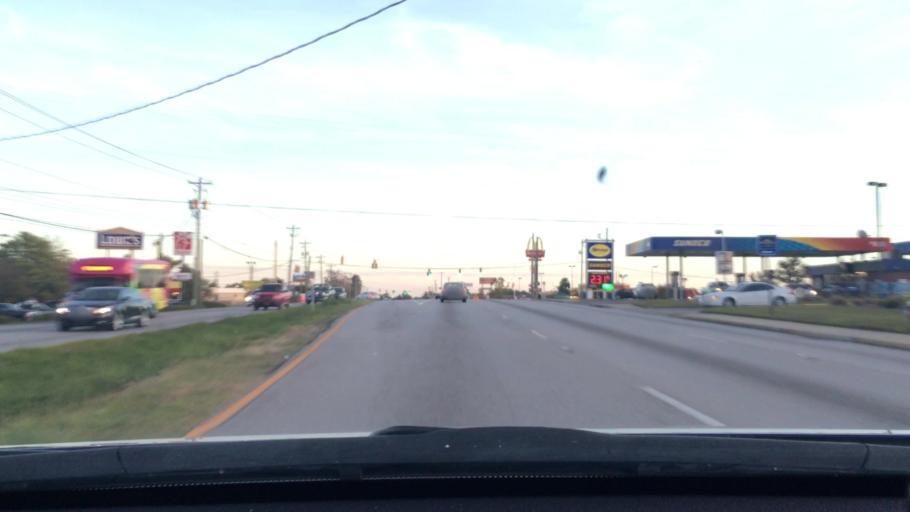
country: US
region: South Carolina
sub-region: Richland County
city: Forest Acres
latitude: 33.9668
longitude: -80.9445
